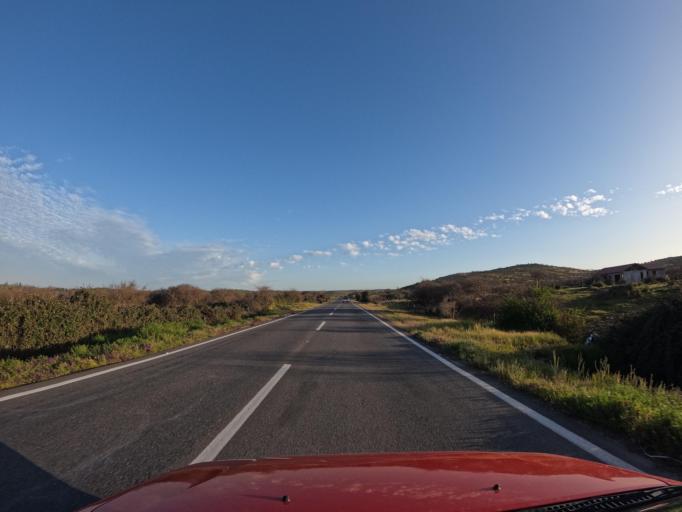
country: CL
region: O'Higgins
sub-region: Provincia de Colchagua
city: Santa Cruz
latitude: -34.2796
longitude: -71.7301
